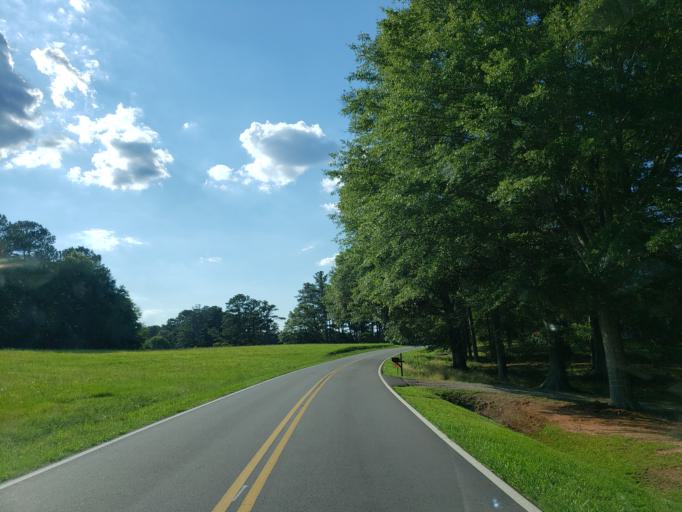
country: US
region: Georgia
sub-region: Haralson County
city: Bremen
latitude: 33.6670
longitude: -85.1151
